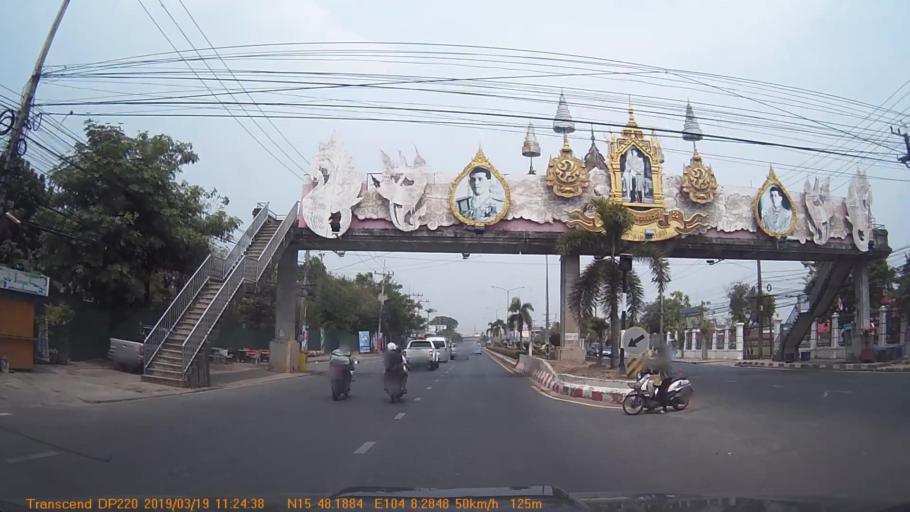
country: TH
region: Yasothon
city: Yasothon
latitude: 15.8032
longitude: 104.1381
